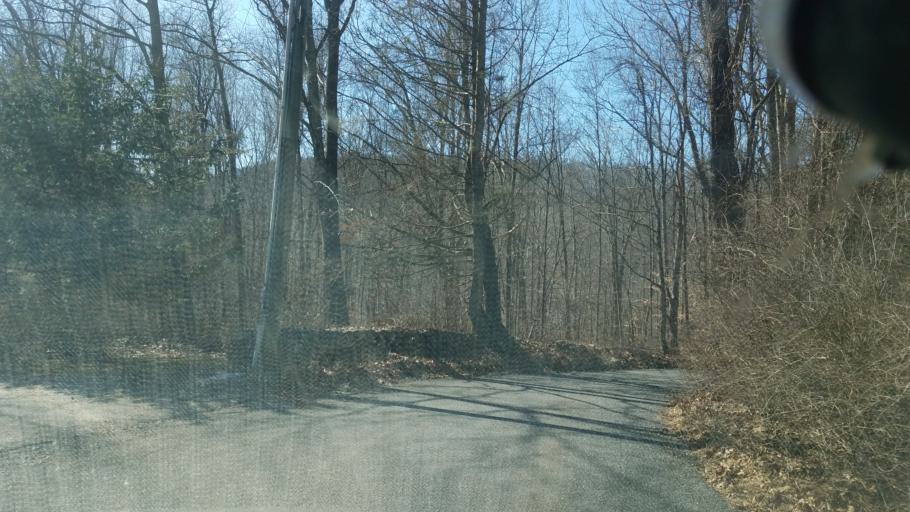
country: US
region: Connecticut
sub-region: Litchfield County
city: New Preston
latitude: 41.6244
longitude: -73.3541
